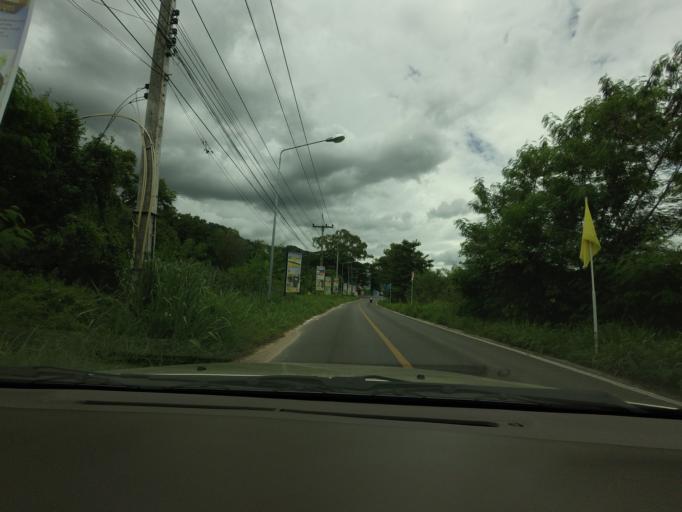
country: TH
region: Chon Buri
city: Ban Bueng
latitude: 13.2152
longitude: 101.0516
